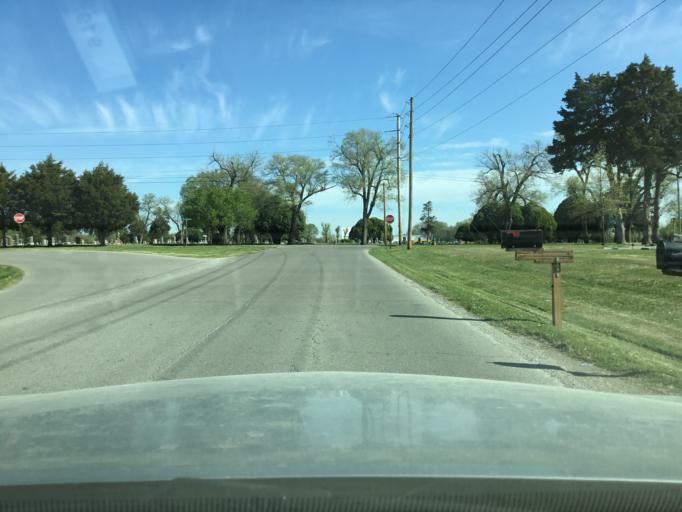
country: US
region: Kansas
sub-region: Neosho County
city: Chanute
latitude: 37.6668
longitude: -95.4434
